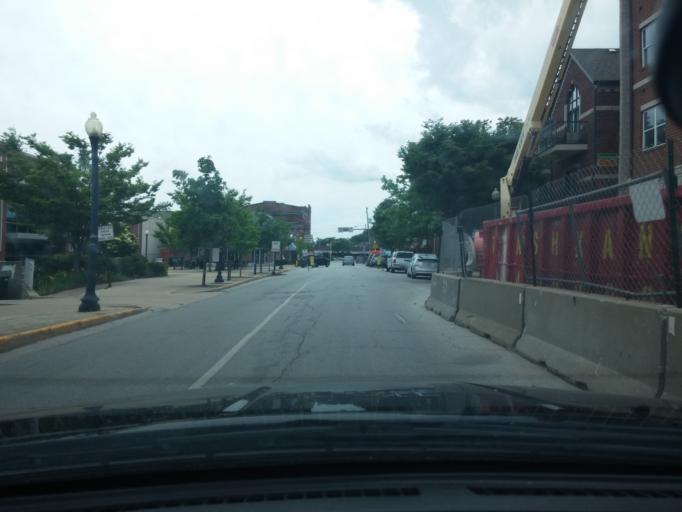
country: US
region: Indiana
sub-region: Tippecanoe County
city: West Lafayette
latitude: 40.4255
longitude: -86.9080
